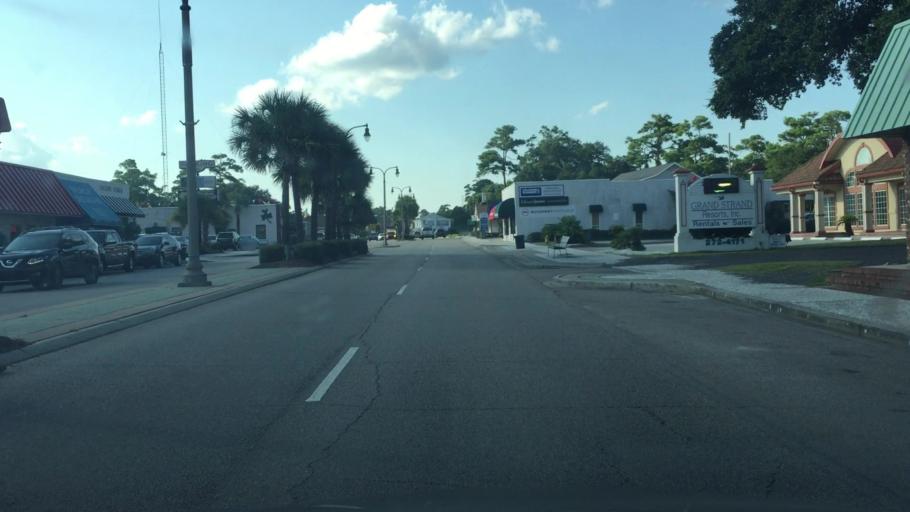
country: US
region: South Carolina
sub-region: Horry County
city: North Myrtle Beach
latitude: 33.8220
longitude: -78.6740
